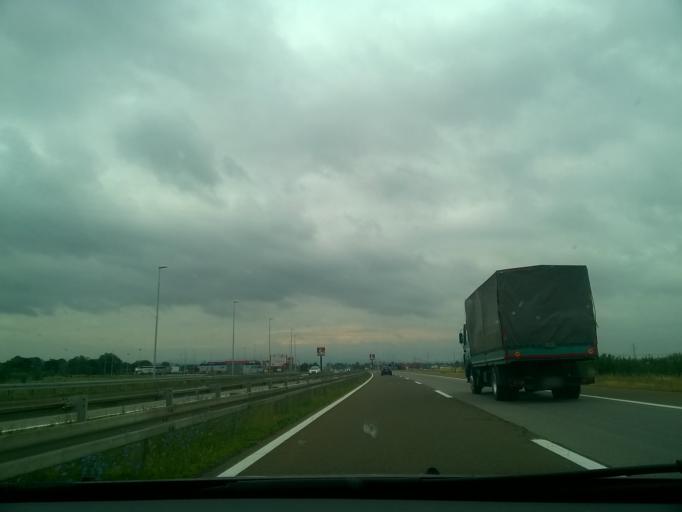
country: RS
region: Central Serbia
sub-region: Pomoravski Okrug
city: Cuprija
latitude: 43.9525
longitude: 21.3698
